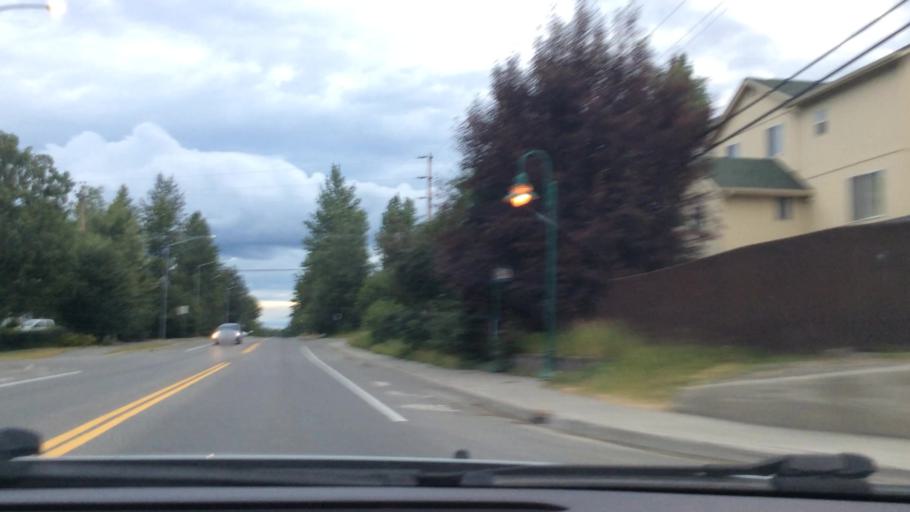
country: US
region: Alaska
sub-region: Anchorage Municipality
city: Elmendorf Air Force Base
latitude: 61.2162
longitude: -149.7559
